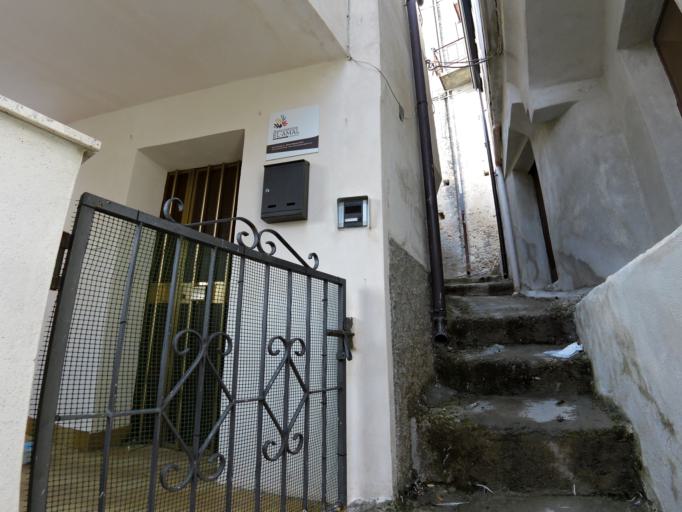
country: IT
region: Calabria
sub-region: Provincia di Reggio Calabria
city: Stignano
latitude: 38.4173
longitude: 16.4702
